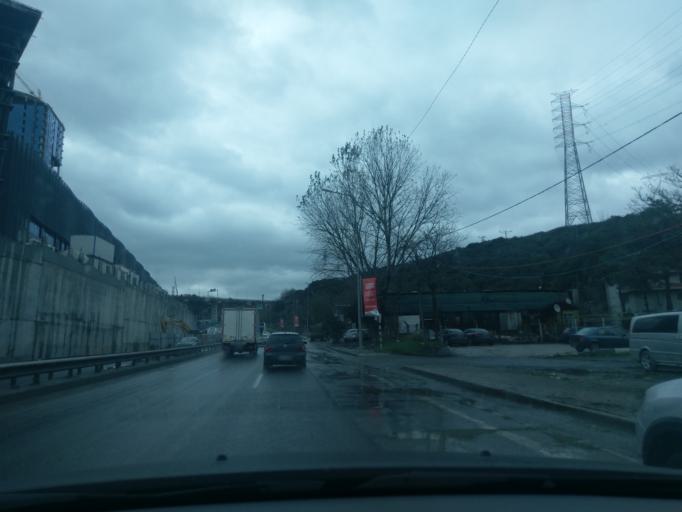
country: TR
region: Istanbul
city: Sisli
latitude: 41.0905
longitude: 28.9540
